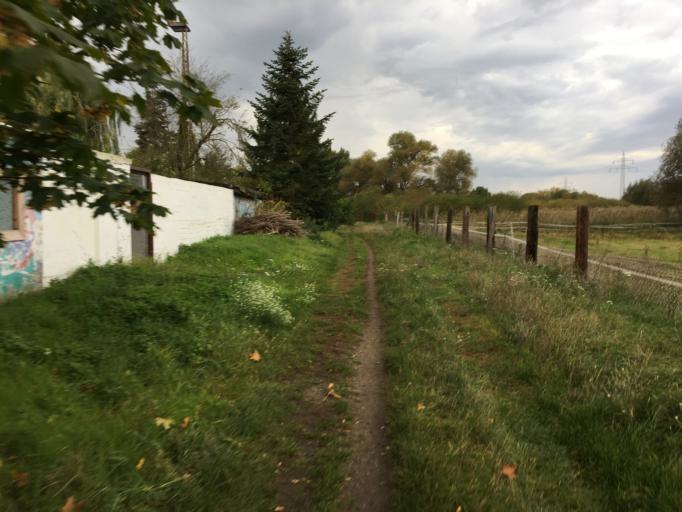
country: DE
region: Lower Saxony
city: Braunschweig
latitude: 52.2979
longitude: 10.5342
